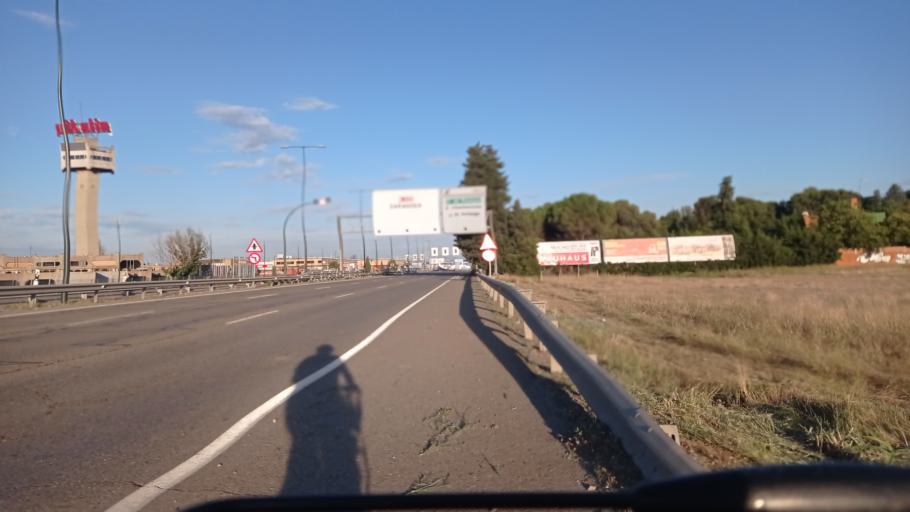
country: ES
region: Aragon
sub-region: Provincia de Zaragoza
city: Oliver-Valdefierro, Oliver, Valdefierro
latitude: 41.6744
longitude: -0.9540
